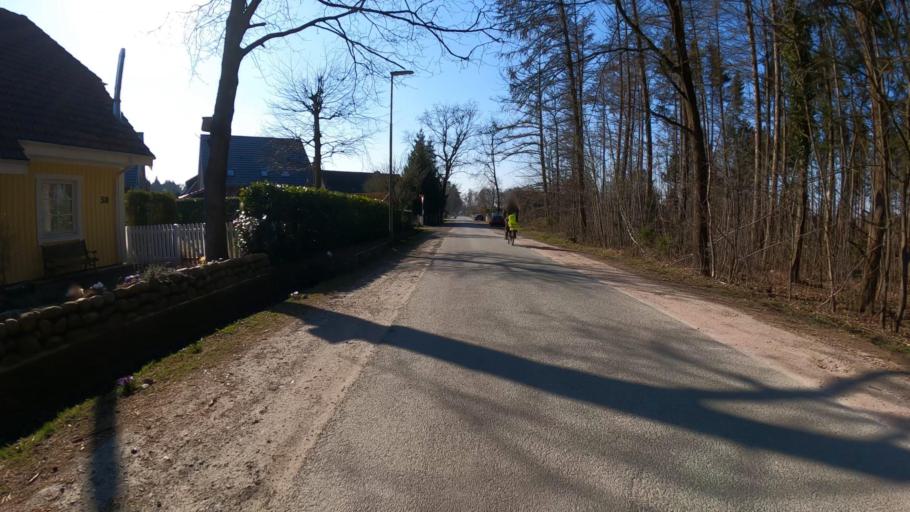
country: DE
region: Lower Saxony
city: Buchholz in der Nordheide
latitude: 53.3098
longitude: 9.8313
